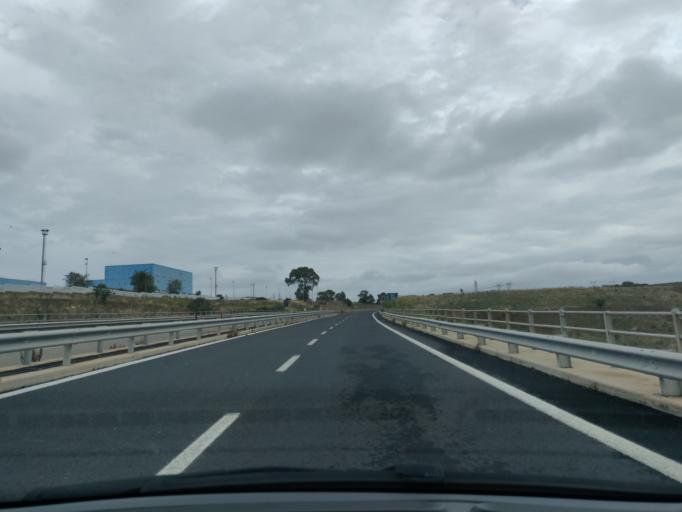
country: IT
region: Latium
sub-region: Citta metropolitana di Roma Capitale
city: Aurelia
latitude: 42.1219
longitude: 11.7910
